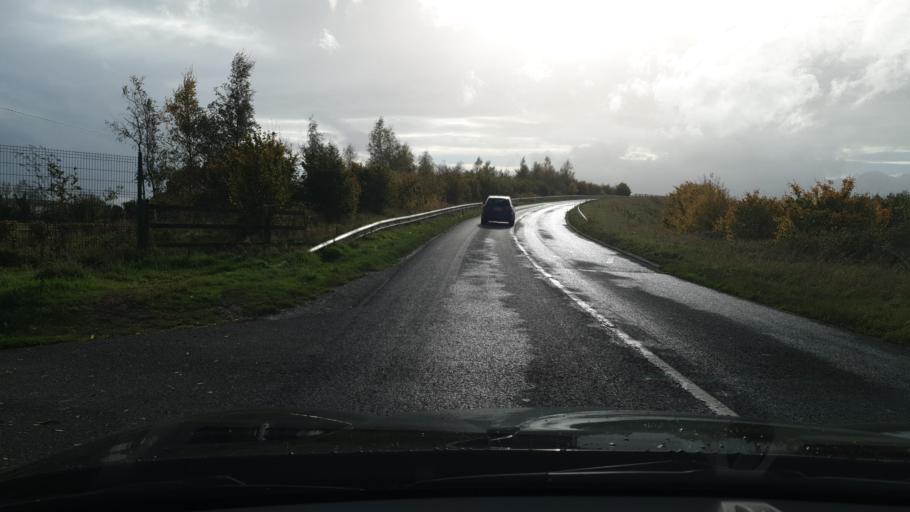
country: IE
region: Leinster
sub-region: An Mhi
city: Ashbourne
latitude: 53.5122
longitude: -6.4191
